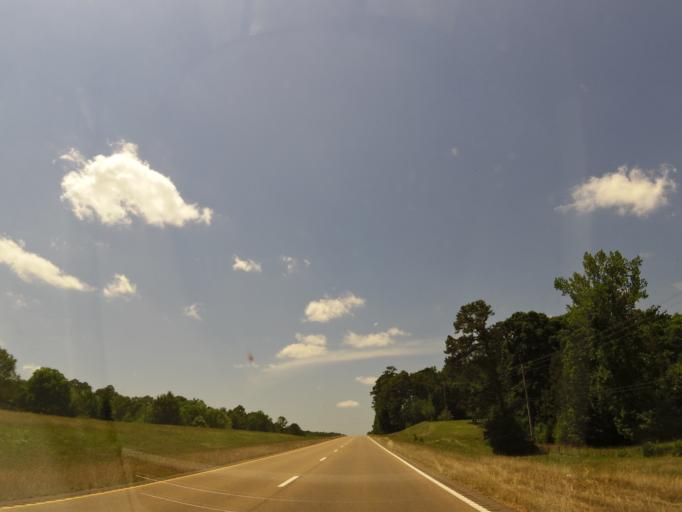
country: US
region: Mississippi
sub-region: Lafayette County
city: Oxford
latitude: 34.3284
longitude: -89.4006
